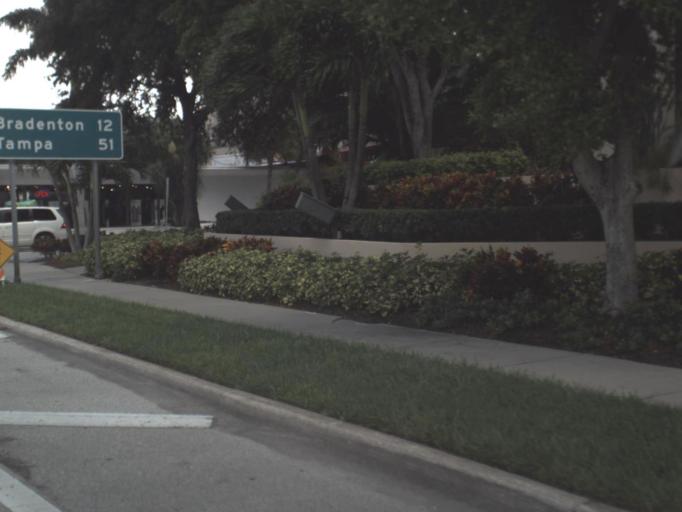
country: US
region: Florida
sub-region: Sarasota County
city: Sarasota
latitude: 27.3364
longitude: -82.5467
